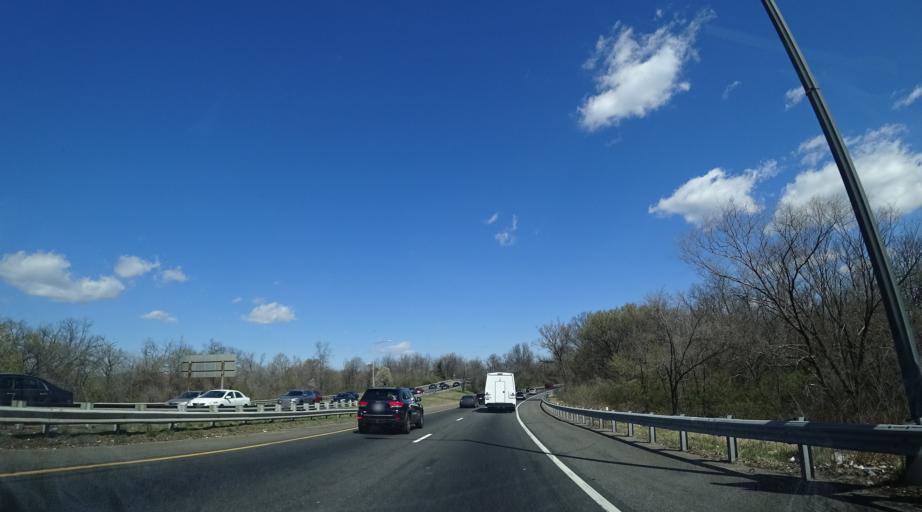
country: US
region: Maryland
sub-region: Prince George's County
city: Coral Hills
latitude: 38.8864
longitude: -76.9624
